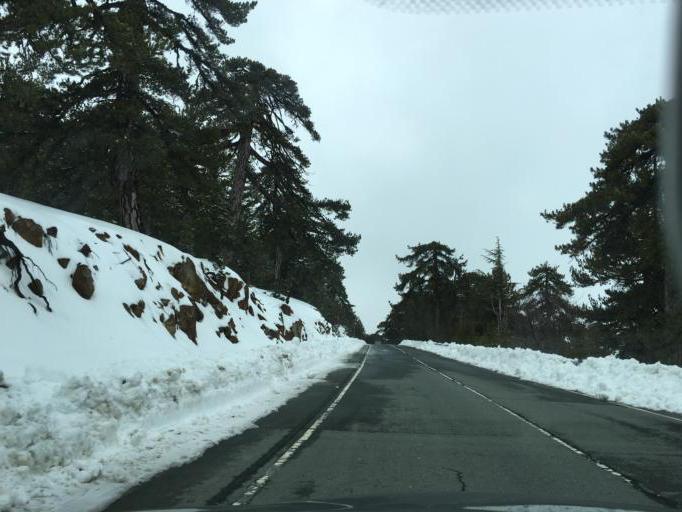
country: CY
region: Lefkosia
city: Kakopetria
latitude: 34.9390
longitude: 32.8691
